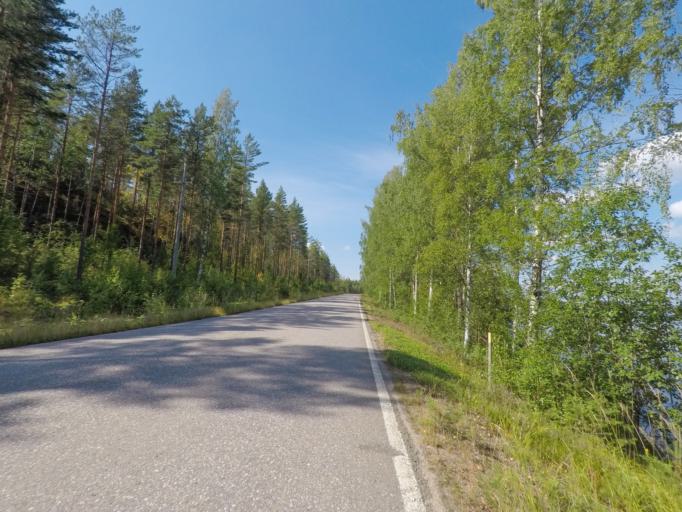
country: FI
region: Southern Savonia
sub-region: Mikkeli
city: Puumala
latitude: 61.4635
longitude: 28.1722
